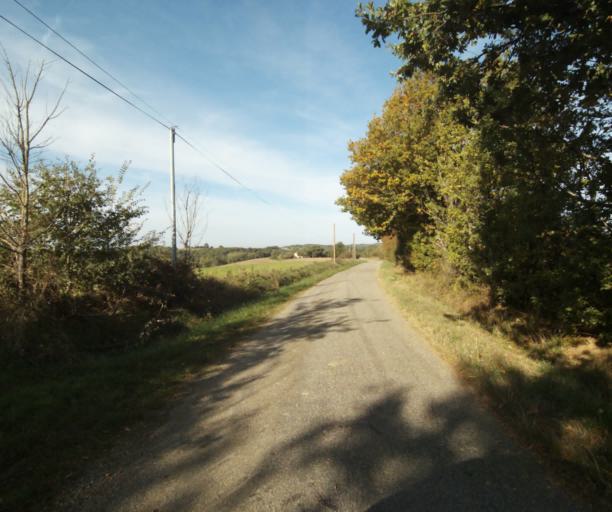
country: FR
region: Midi-Pyrenees
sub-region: Departement du Tarn-et-Garonne
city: Nohic
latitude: 43.9257
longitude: 1.4548
